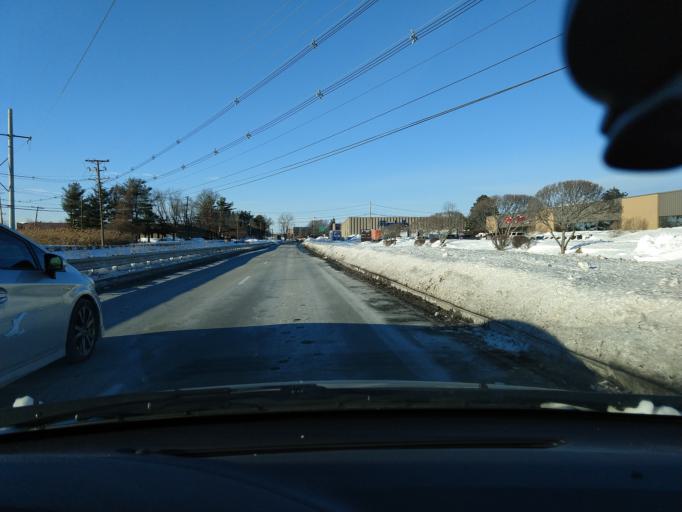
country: US
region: Massachusetts
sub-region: Middlesex County
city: Woburn
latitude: 42.5114
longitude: -71.1335
